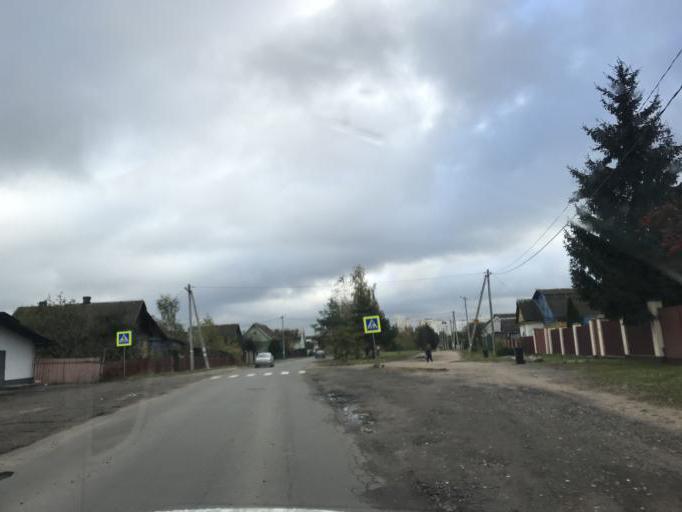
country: BY
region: Mogilev
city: Mahilyow
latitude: 53.8842
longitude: 30.3453
